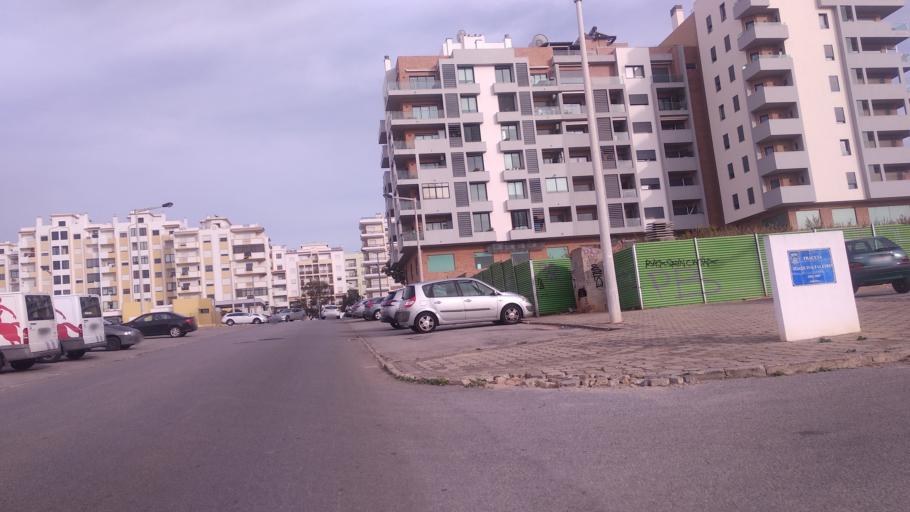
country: PT
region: Faro
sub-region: Faro
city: Faro
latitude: 37.0263
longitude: -7.9377
